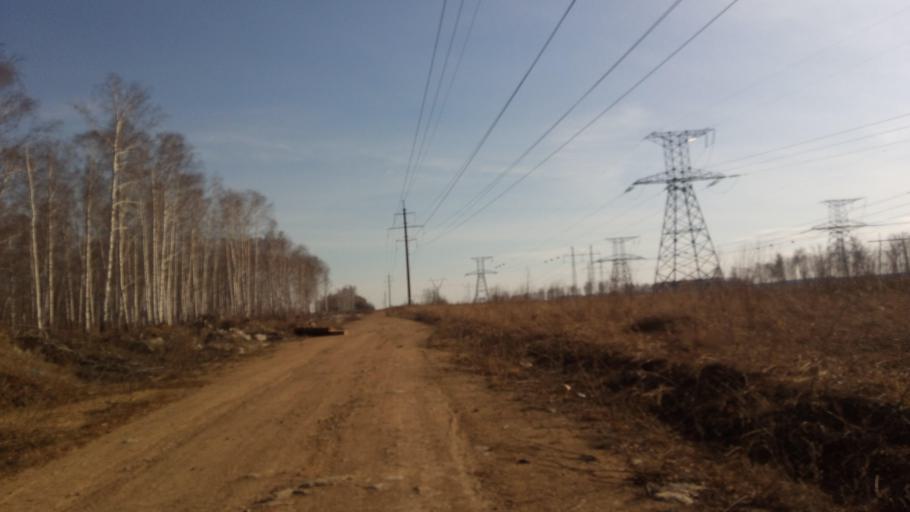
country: RU
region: Chelyabinsk
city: Sargazy
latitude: 55.1176
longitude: 61.2366
